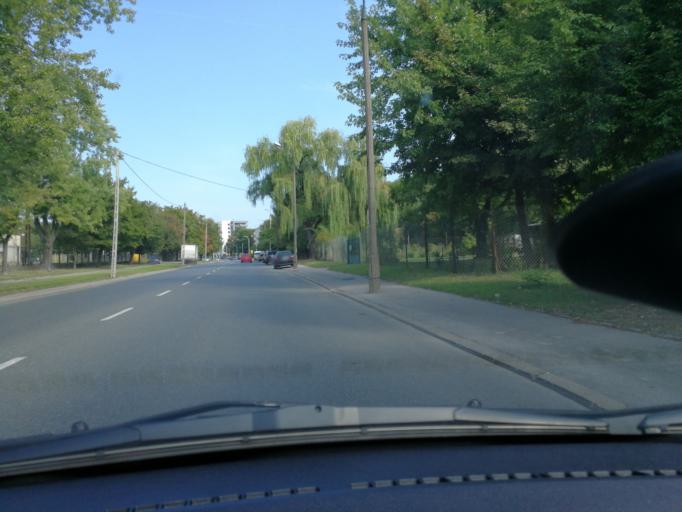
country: PL
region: Masovian Voivodeship
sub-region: Warszawa
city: Bemowo
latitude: 52.2312
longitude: 20.9419
